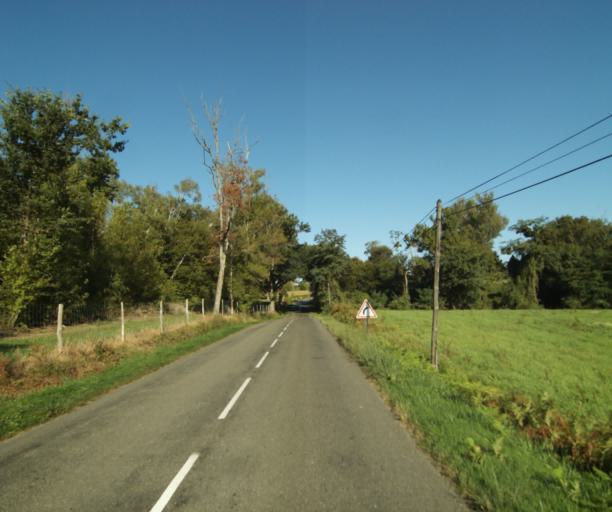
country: FR
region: Aquitaine
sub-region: Departement des Landes
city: Gabarret
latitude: 43.9279
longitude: 0.0173
